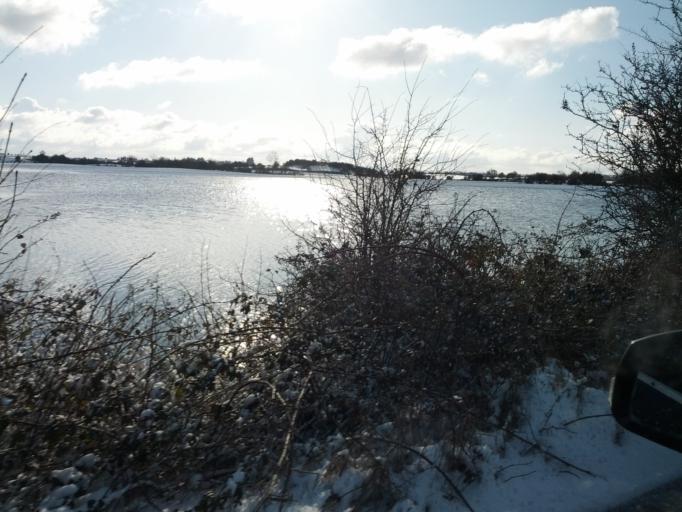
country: IE
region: Connaught
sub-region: County Galway
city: Athenry
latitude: 53.2037
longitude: -8.7716
